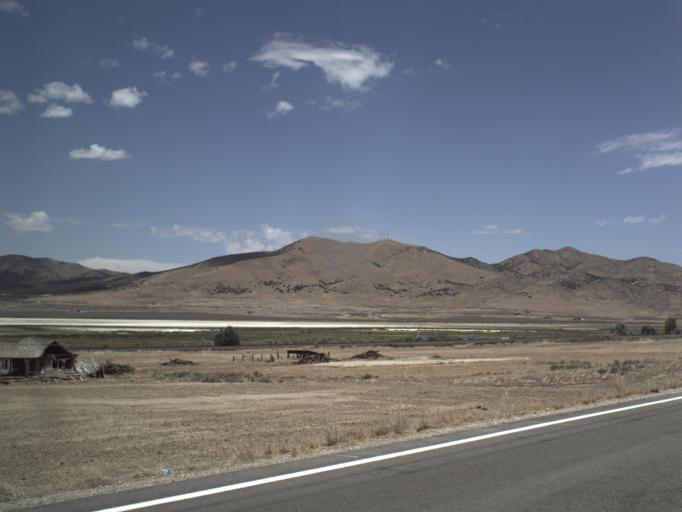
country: US
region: Utah
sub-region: Tooele County
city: Tooele
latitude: 40.4125
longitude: -112.3839
